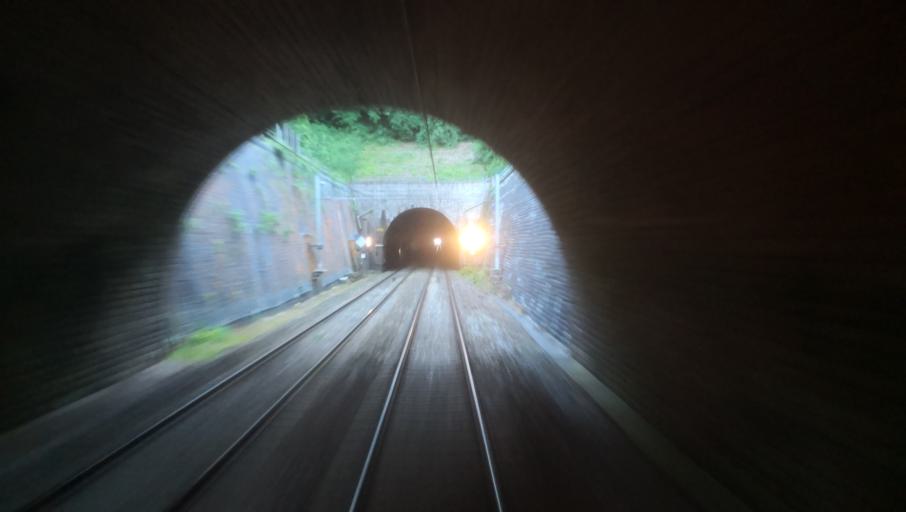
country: FR
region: Ile-de-France
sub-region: Departement des Yvelines
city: Breval
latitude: 48.9536
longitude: 1.5698
